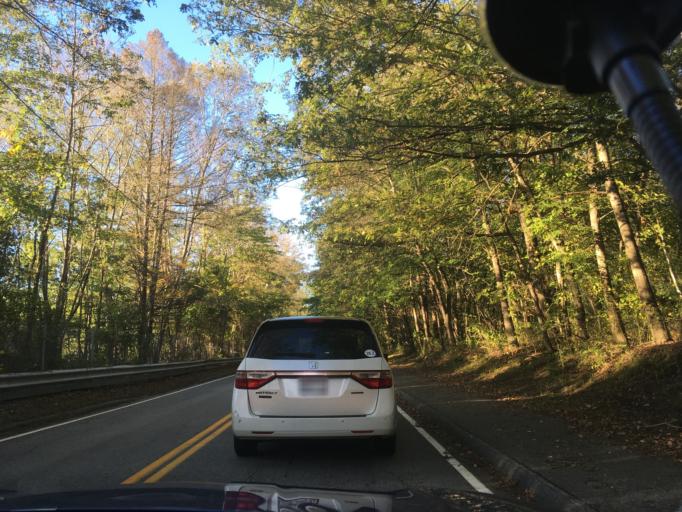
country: US
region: Rhode Island
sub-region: Kent County
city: East Greenwich
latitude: 41.6422
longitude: -71.4868
